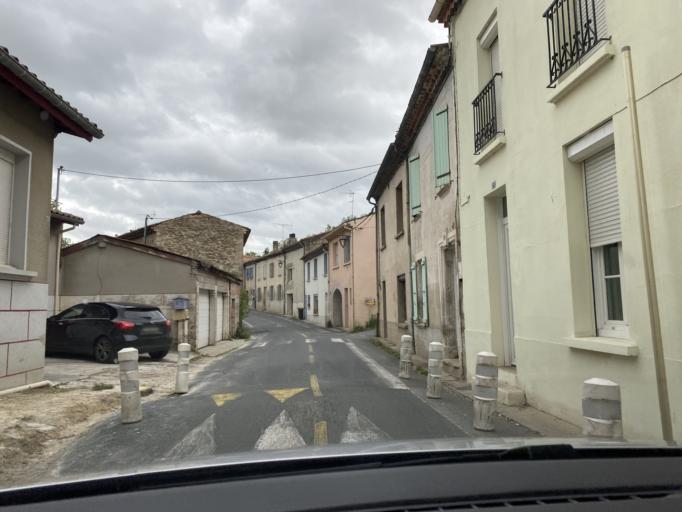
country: FR
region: Midi-Pyrenees
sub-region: Departement du Tarn
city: Saix
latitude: 43.5807
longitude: 2.1833
